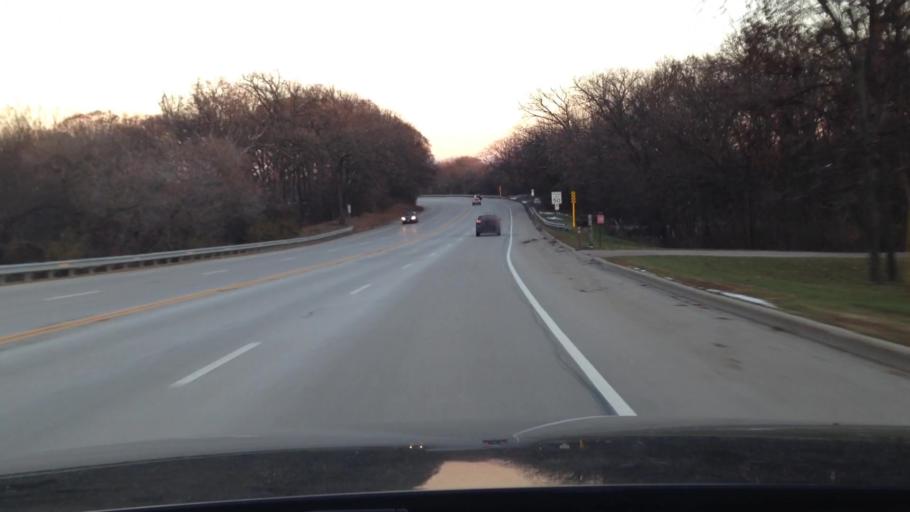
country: US
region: Illinois
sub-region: DuPage County
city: Wayne
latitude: 41.9453
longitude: -88.2036
